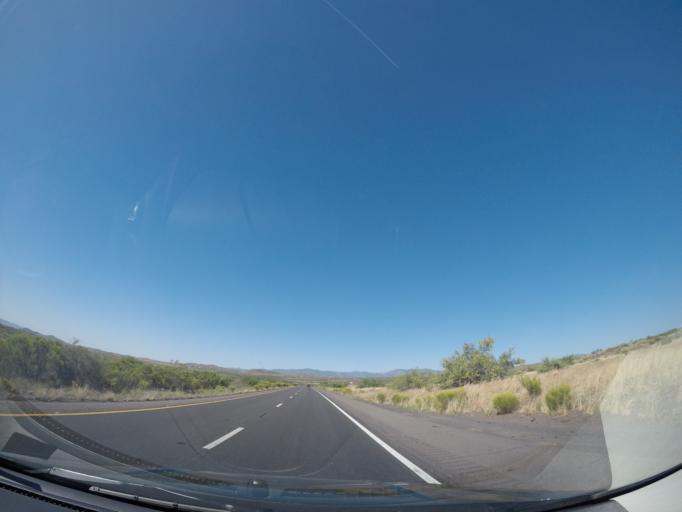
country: US
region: Arizona
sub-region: Yavapai County
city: Spring Valley
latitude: 34.3724
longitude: -112.1096
